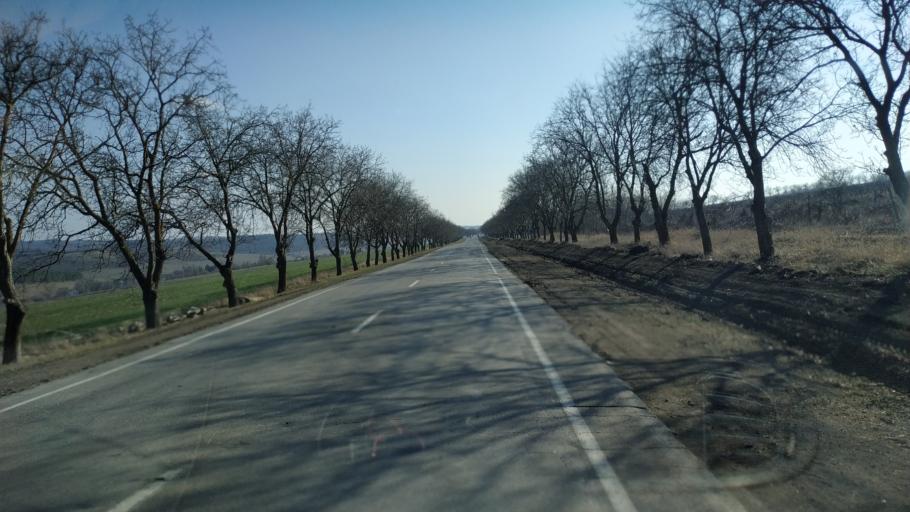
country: MD
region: Hincesti
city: Hincesti
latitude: 46.7865
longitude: 28.5240
